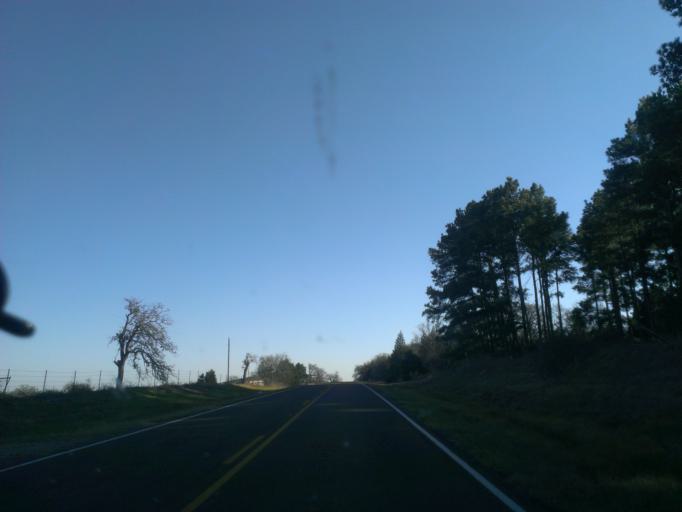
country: US
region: Texas
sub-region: Bastrop County
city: Elgin
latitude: 30.4002
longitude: -97.2495
